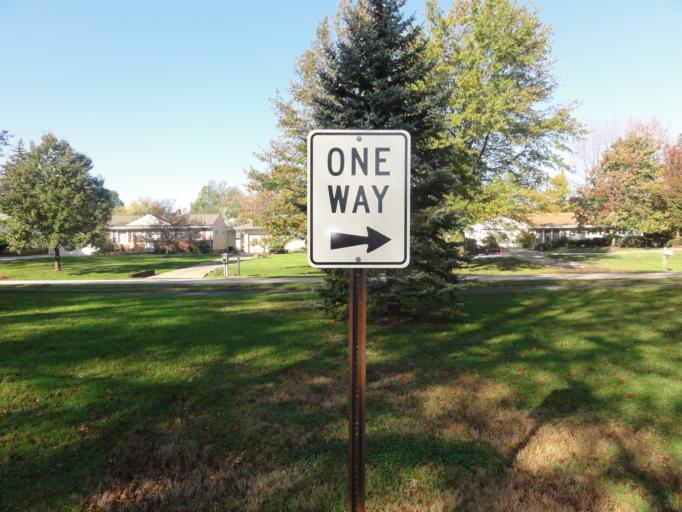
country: US
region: Ohio
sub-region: Cuyahoga County
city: Middleburg Heights
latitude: 41.3462
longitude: -81.8292
